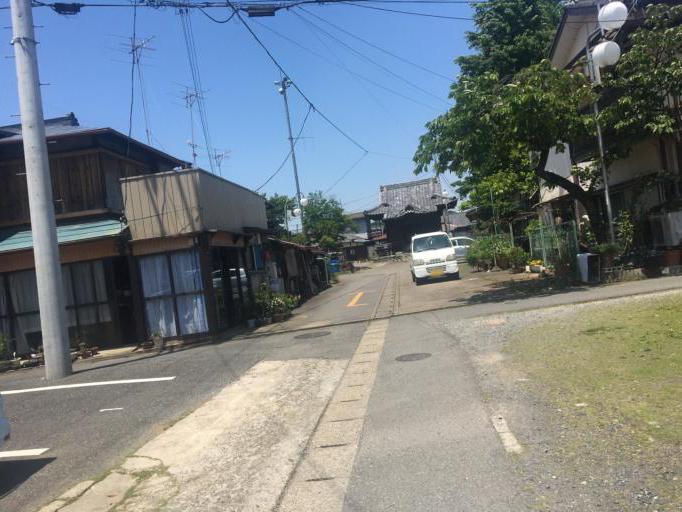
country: JP
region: Saitama
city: Ogawa
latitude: 36.0540
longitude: 139.2566
